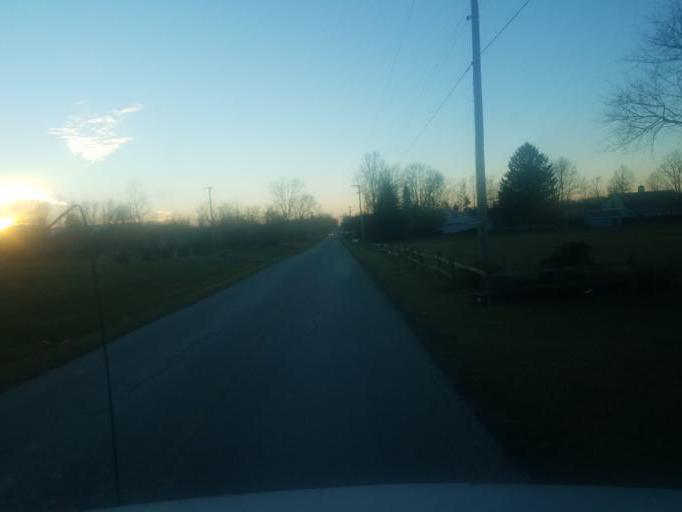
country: US
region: Ohio
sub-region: Richland County
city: Ontario
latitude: 40.8430
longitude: -82.5803
